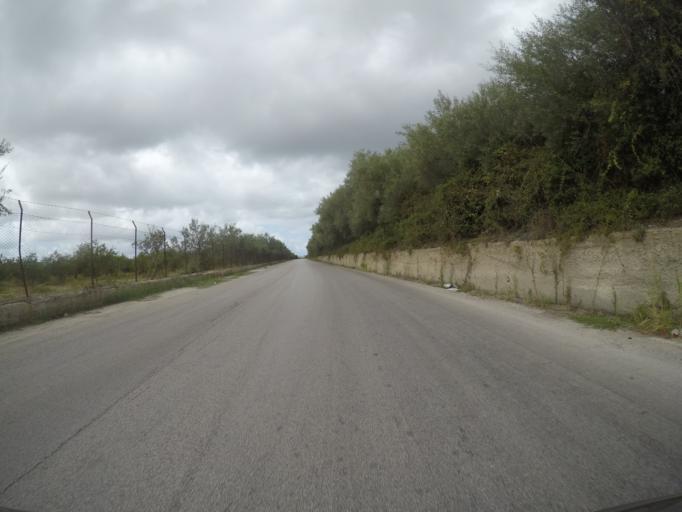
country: IT
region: Sicily
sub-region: Palermo
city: Partinico
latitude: 38.0862
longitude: 13.1129
